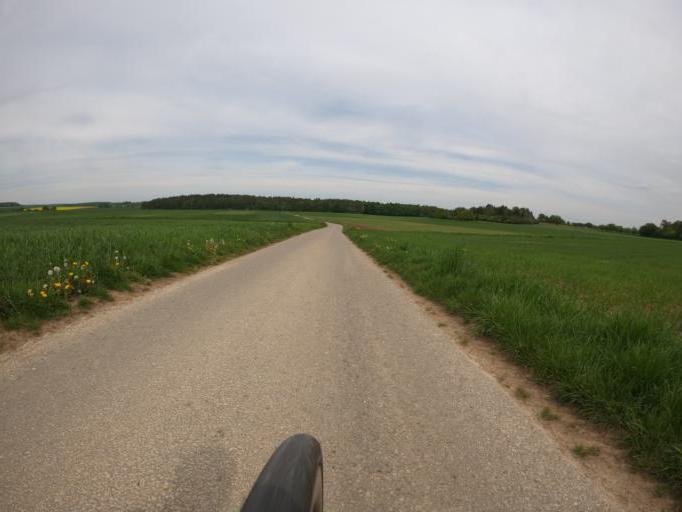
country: DE
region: Baden-Wuerttemberg
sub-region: Regierungsbezirk Stuttgart
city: Aidlingen
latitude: 48.6982
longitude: 8.8716
